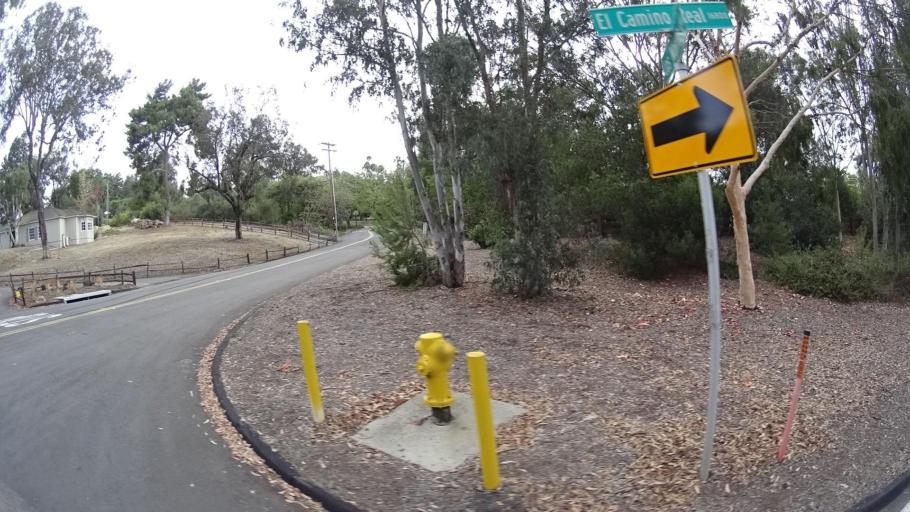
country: US
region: California
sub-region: San Diego County
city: Rancho Santa Fe
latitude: 33.0168
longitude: -117.2393
